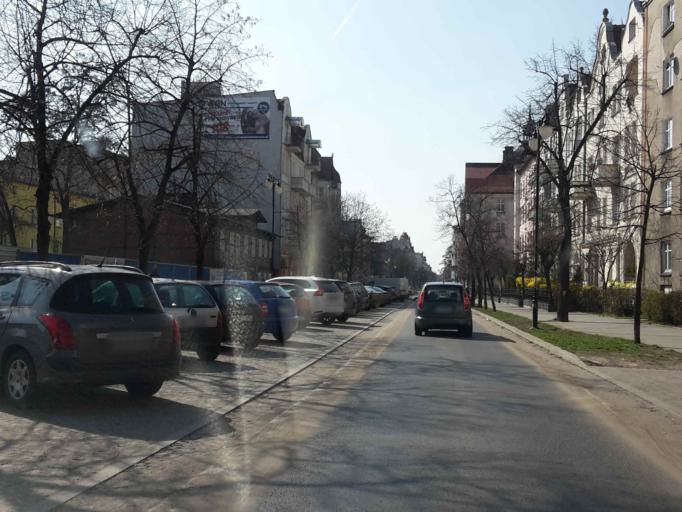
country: PL
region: Kujawsko-Pomorskie
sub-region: Torun
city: Torun
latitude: 53.0120
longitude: 18.5878
